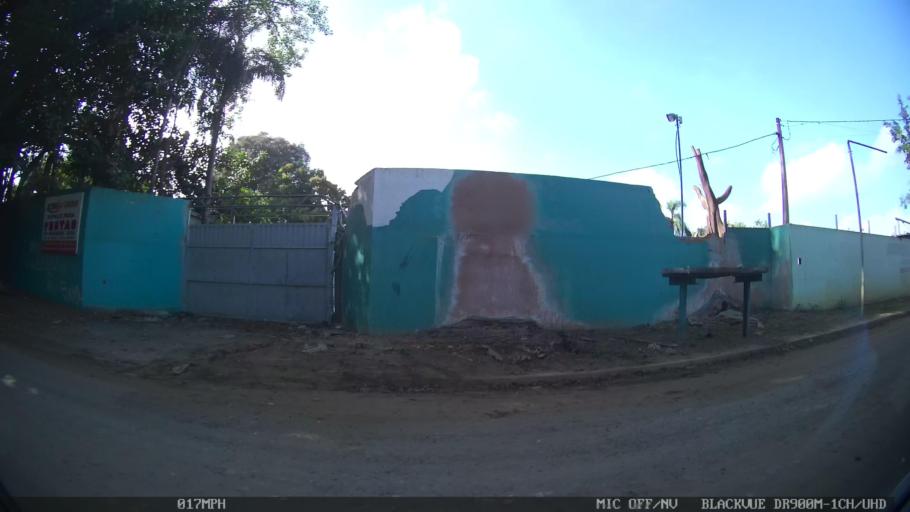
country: BR
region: Sao Paulo
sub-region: Hortolandia
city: Hortolandia
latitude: -22.9069
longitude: -47.1721
